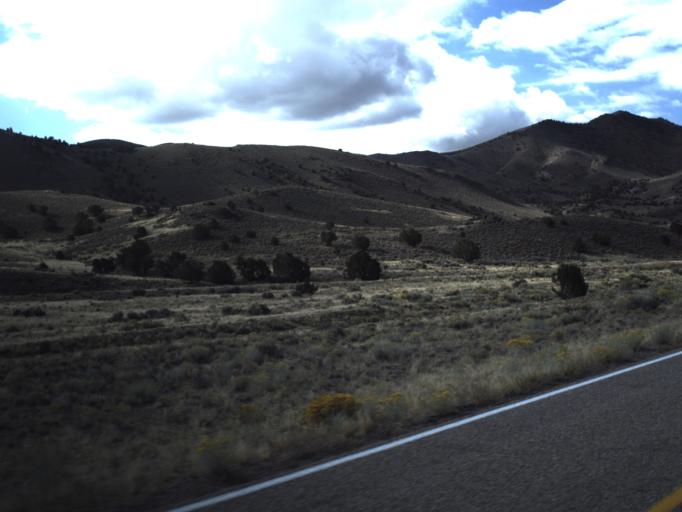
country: US
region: Utah
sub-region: Beaver County
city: Milford
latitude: 38.4436
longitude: -113.2654
